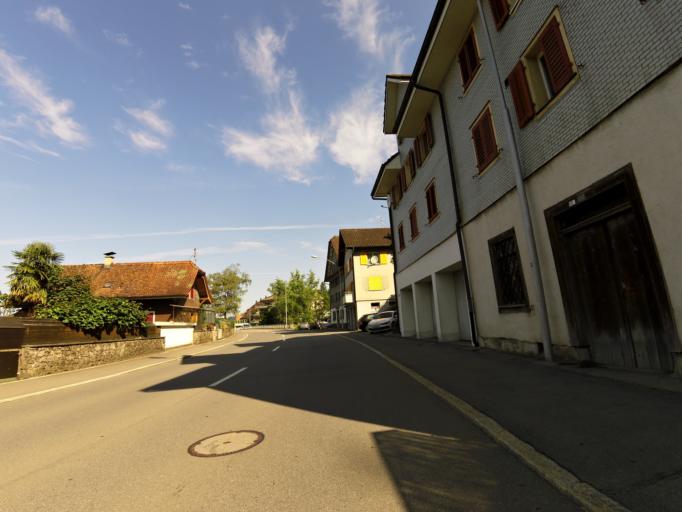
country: CH
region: Zug
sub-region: Zug
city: Walchwil
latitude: 47.0948
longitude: 8.5190
